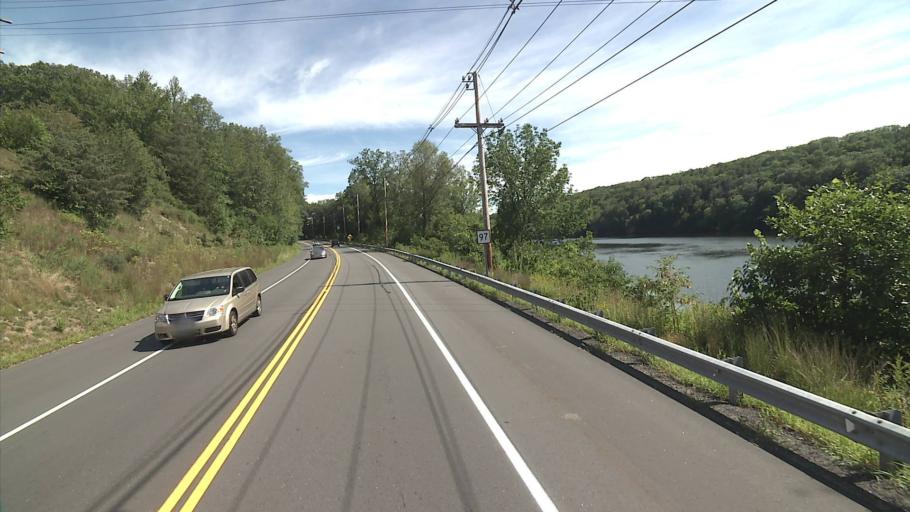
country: US
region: Connecticut
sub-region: New London County
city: Lisbon
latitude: 41.5762
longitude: -72.0456
